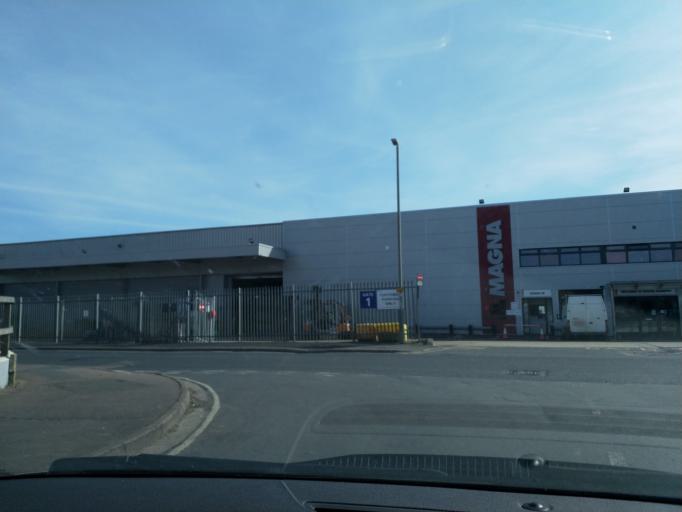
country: GB
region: England
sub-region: Oxfordshire
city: Banbury
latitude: 52.0765
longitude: -1.3403
